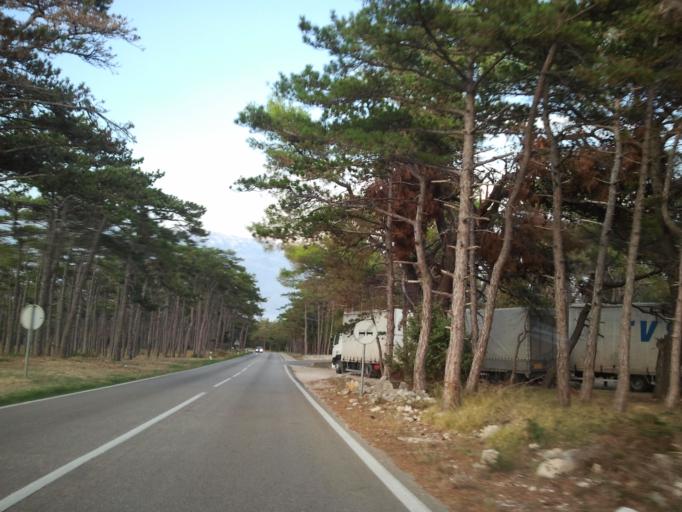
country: HR
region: Zadarska
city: Razanac
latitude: 44.2758
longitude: 15.3405
